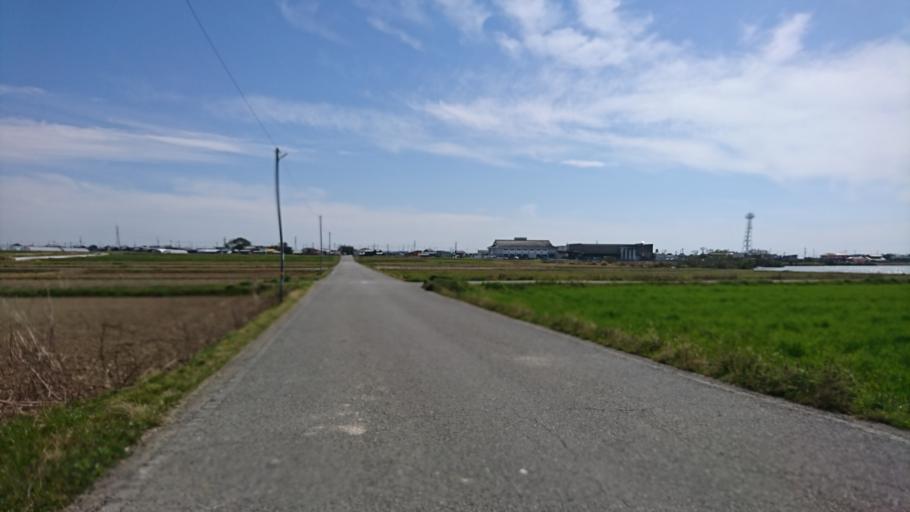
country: JP
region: Hyogo
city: Miki
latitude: 34.7588
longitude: 134.9342
